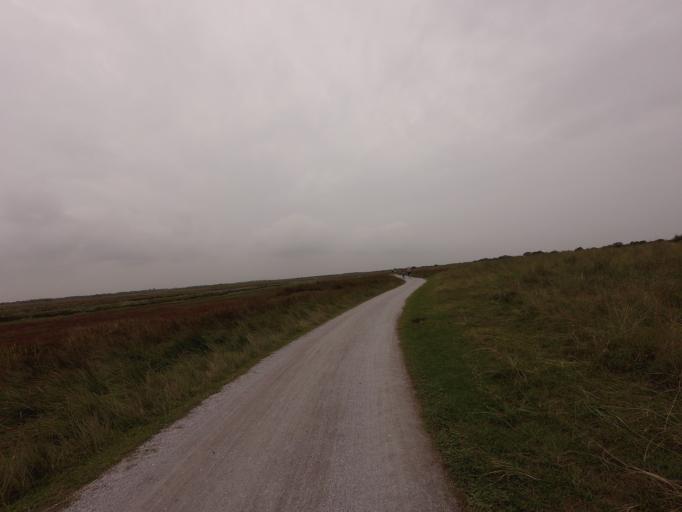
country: NL
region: Friesland
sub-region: Gemeente Schiermonnikoog
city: Schiermonnikoog
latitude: 53.4863
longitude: 6.2138
